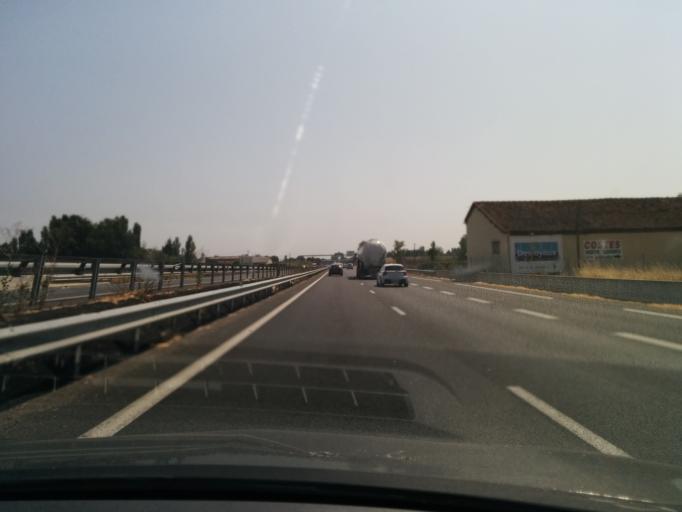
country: FR
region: Midi-Pyrenees
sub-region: Departement du Tarn
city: Marssac-sur-Tarn
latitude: 43.9151
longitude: 2.0618
